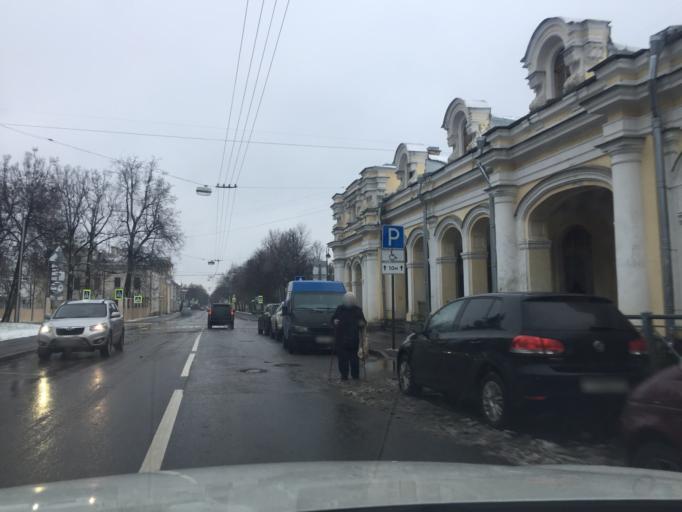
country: RU
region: St.-Petersburg
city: Pushkin
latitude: 59.7199
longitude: 30.4038
